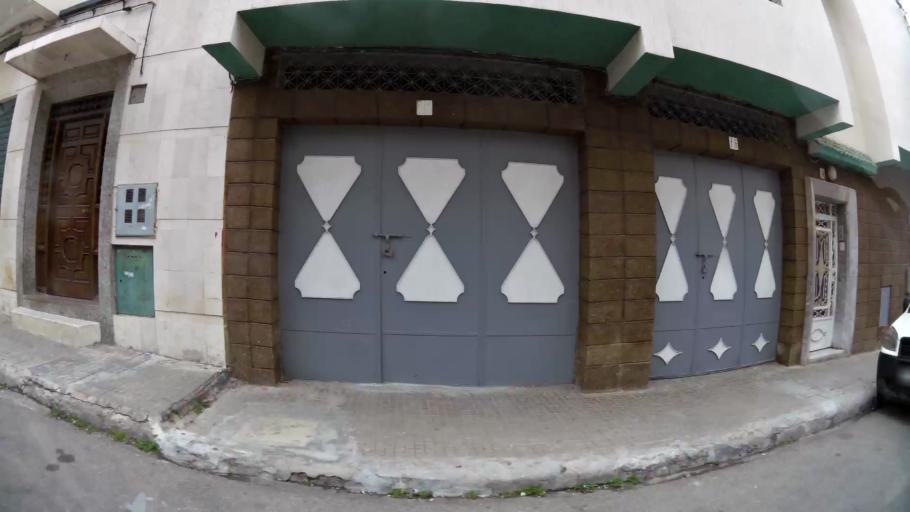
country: MA
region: Tanger-Tetouan
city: Tetouan
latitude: 35.5777
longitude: -5.3544
